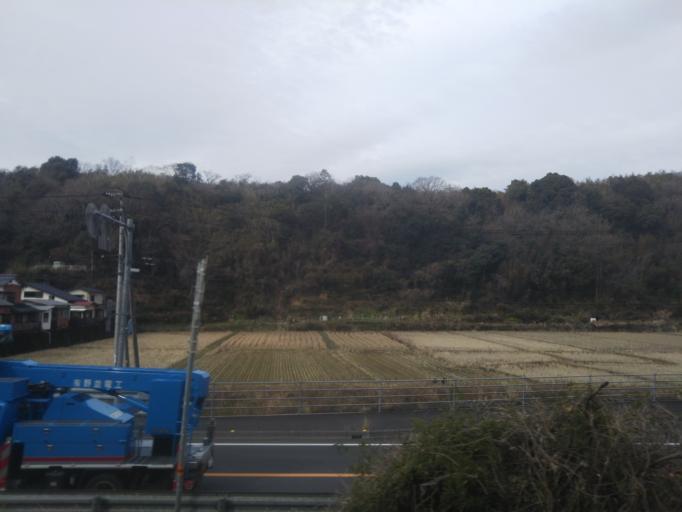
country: JP
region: Kochi
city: Nakamura
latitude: 32.9900
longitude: 132.9630
